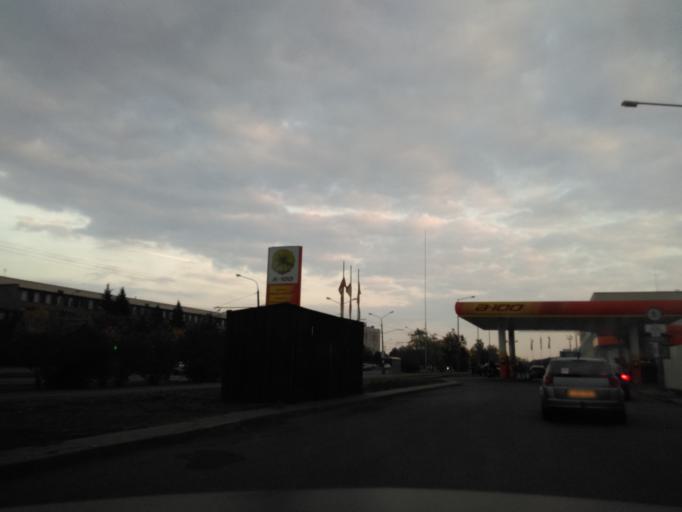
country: BY
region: Minsk
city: Vyaliki Trastsyanets
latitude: 53.8914
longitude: 27.6457
